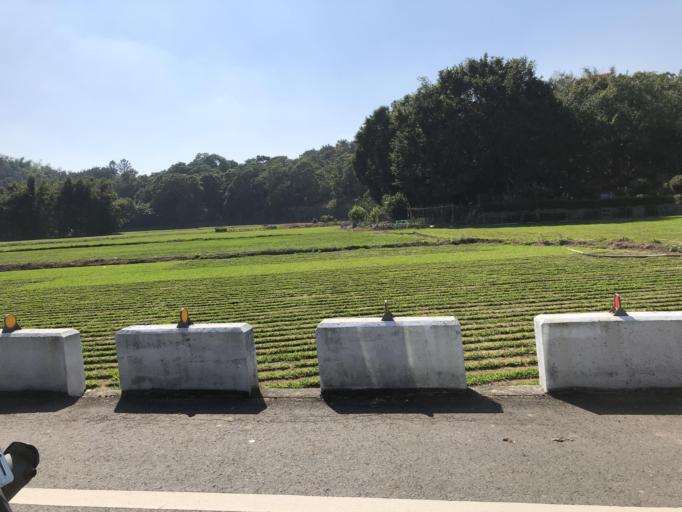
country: TW
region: Taiwan
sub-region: Tainan
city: Tainan
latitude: 23.0340
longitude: 120.3474
